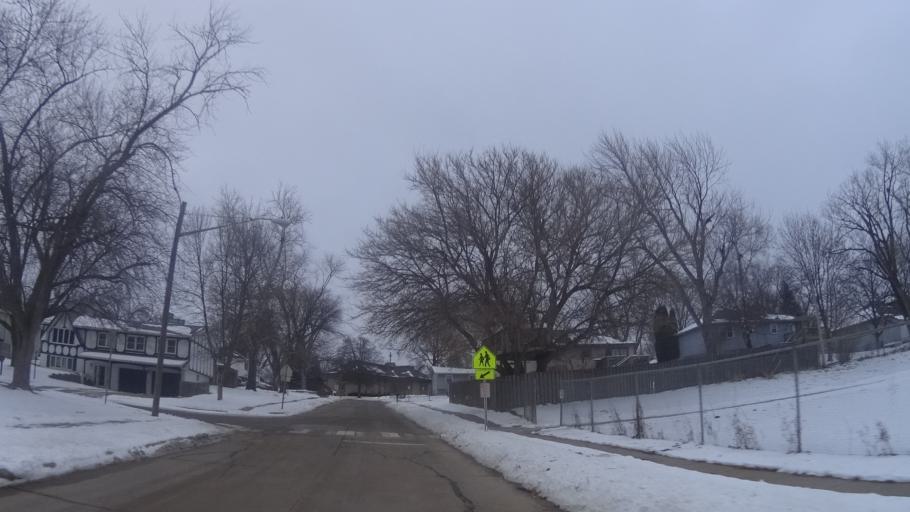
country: US
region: Nebraska
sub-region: Sarpy County
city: Offutt Air Force Base
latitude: 41.1457
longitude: -95.9245
